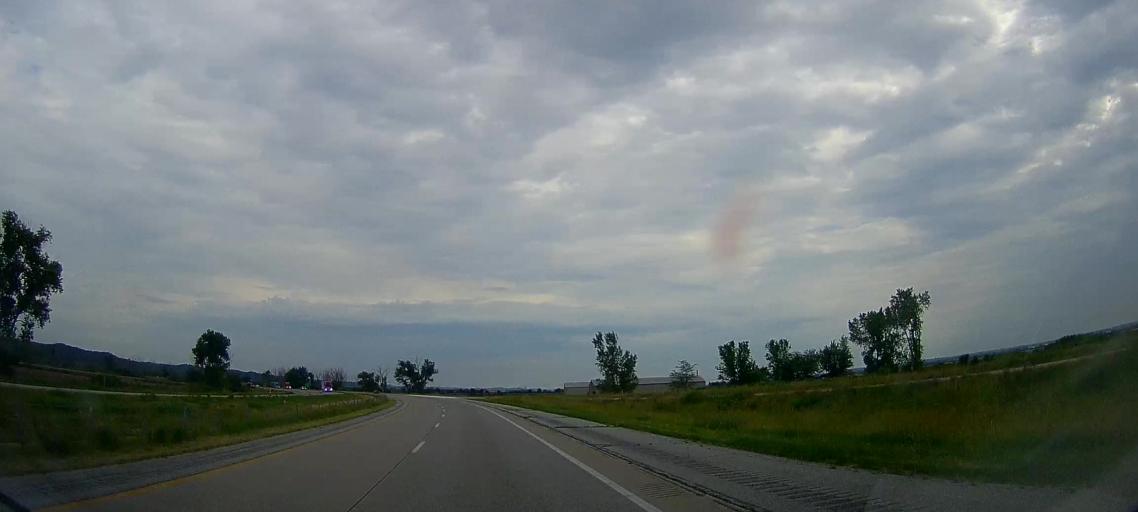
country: US
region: Iowa
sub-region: Harrison County
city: Missouri Valley
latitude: 41.5172
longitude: -95.9169
